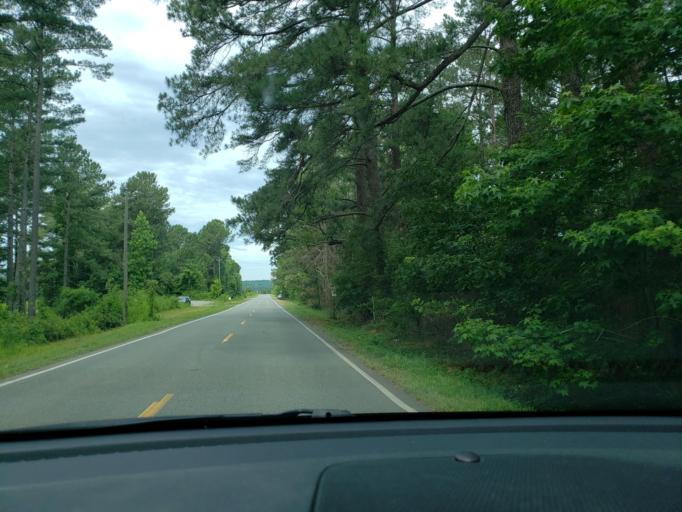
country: US
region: North Carolina
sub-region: Chatham County
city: Fearrington Village
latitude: 35.7895
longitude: -79.0036
